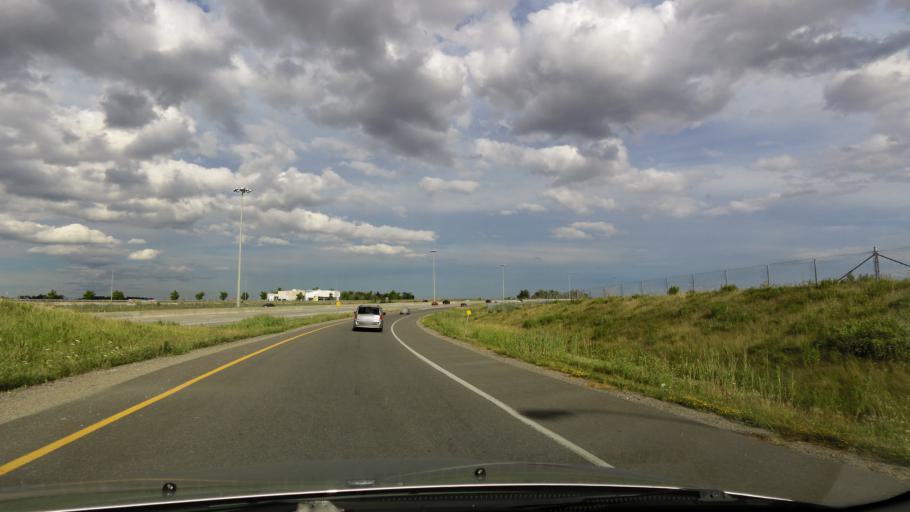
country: CA
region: Ontario
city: Brampton
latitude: 43.7559
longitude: -79.7977
